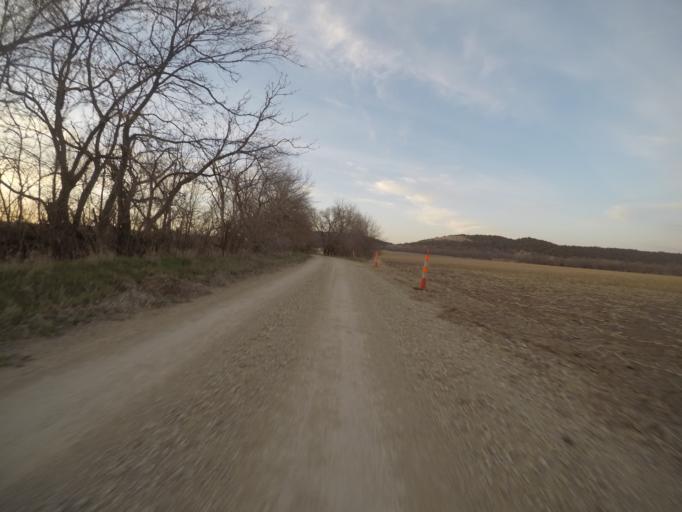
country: US
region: Kansas
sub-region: Riley County
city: Ogden
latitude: 39.1608
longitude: -96.6678
